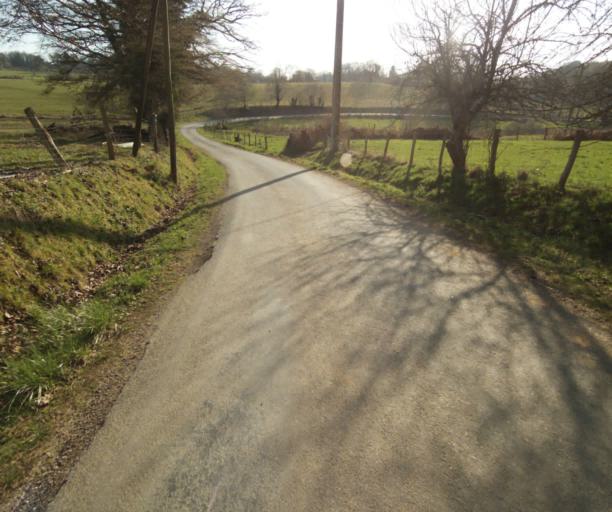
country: FR
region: Limousin
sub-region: Departement de la Correze
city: Saint-Mexant
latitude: 45.3418
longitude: 1.6165
